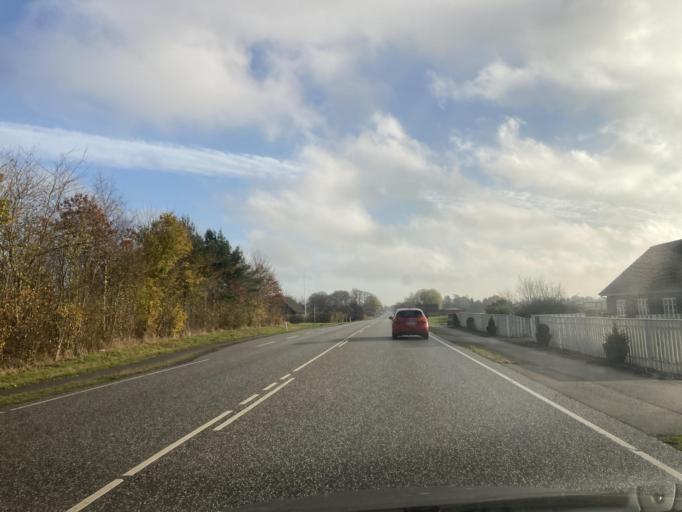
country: DK
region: Zealand
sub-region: Guldborgsund Kommune
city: Sakskobing
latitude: 54.7761
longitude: 11.7298
